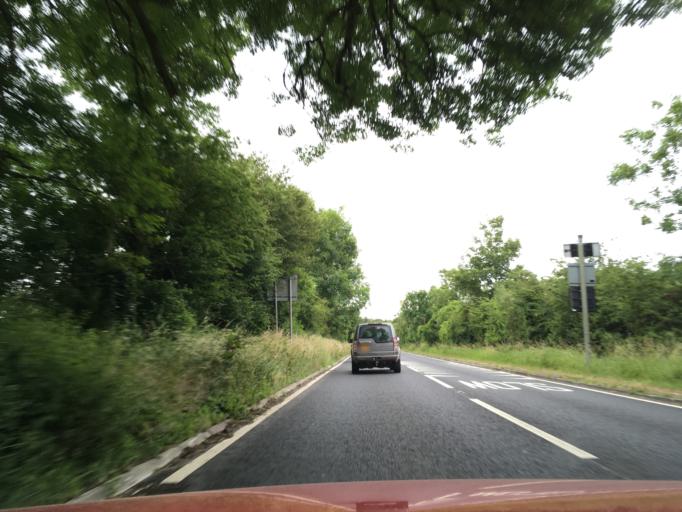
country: GB
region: England
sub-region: Gloucestershire
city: Shipton Village
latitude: 51.8826
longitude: -1.9797
